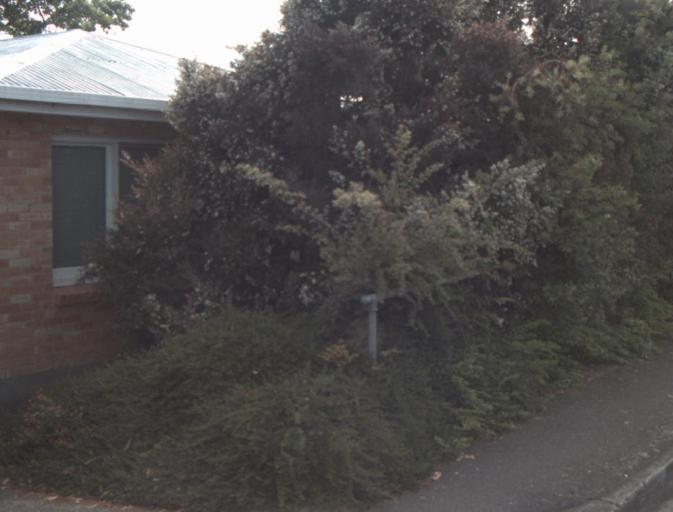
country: AU
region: Tasmania
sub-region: Launceston
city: Summerhill
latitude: -41.4720
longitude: 147.1308
